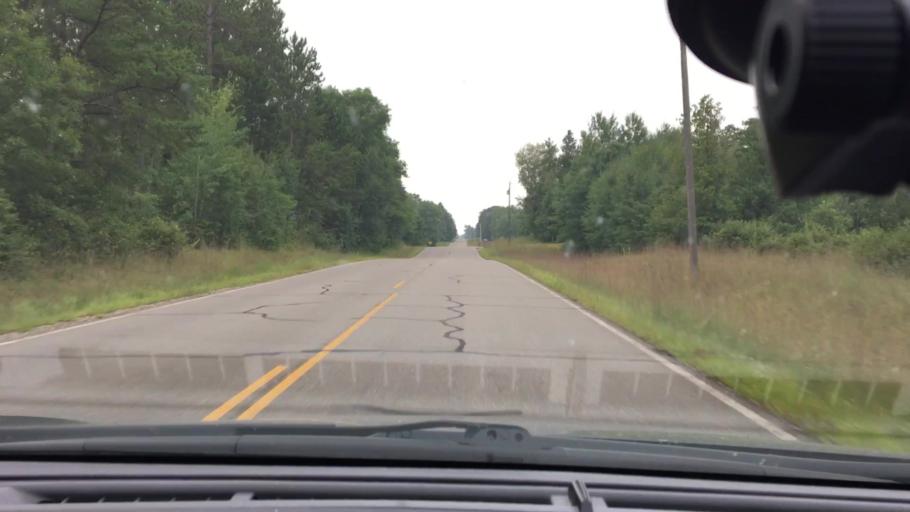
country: US
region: Minnesota
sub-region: Crow Wing County
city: Cross Lake
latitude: 46.6551
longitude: -94.0094
